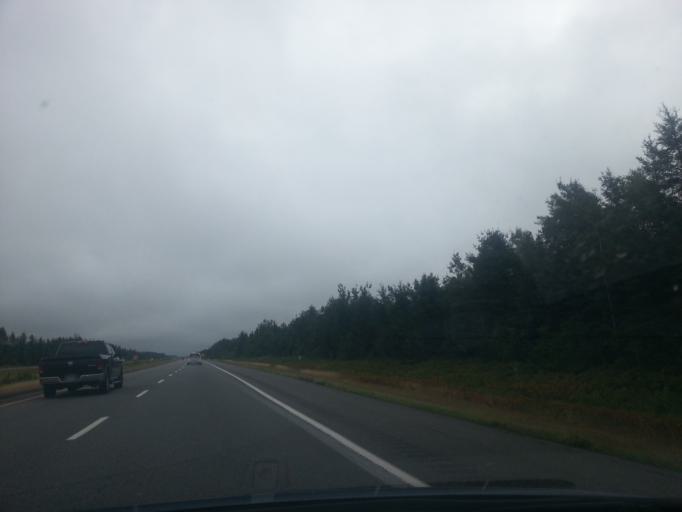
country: CA
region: Quebec
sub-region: Mauricie
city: Daveluyville
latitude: 46.2713
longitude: -72.0121
